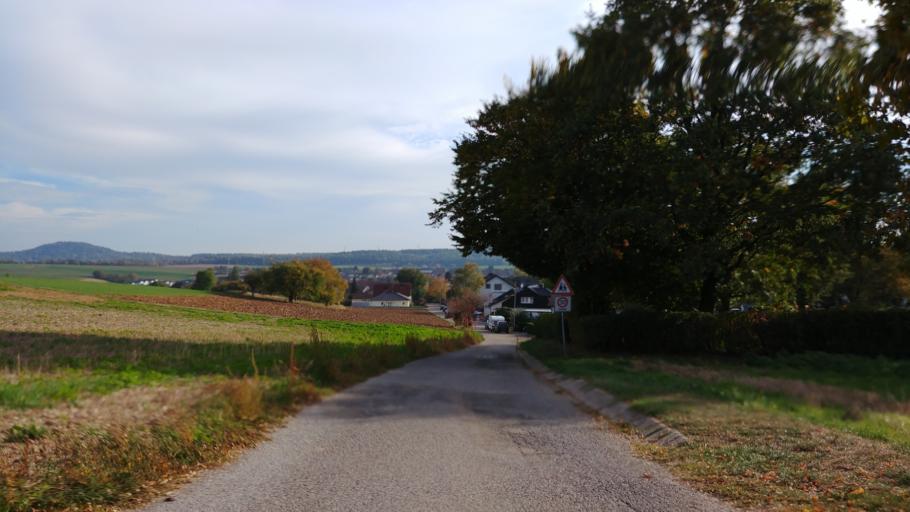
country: DE
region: Baden-Wuerttemberg
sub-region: Regierungsbezirk Stuttgart
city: Ilsfeld
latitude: 49.0617
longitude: 9.2485
